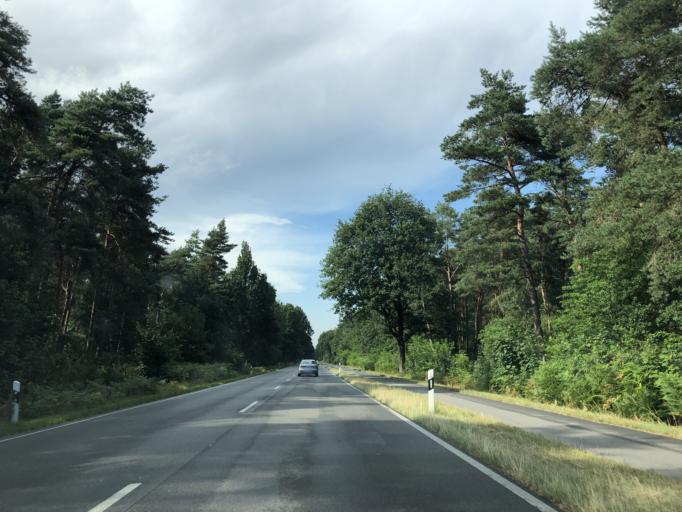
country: DE
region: North Rhine-Westphalia
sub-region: Regierungsbezirk Dusseldorf
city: Kranenburg
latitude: 51.7283
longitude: 6.0367
